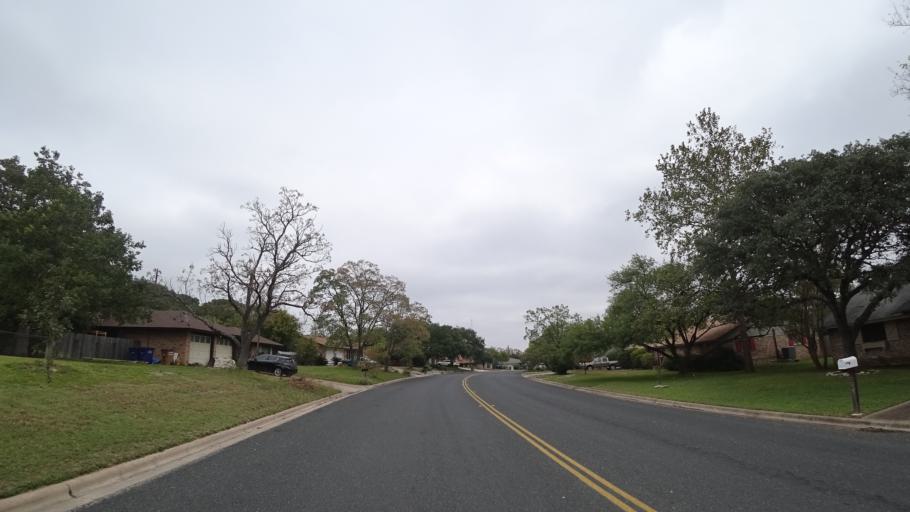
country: US
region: Texas
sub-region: Travis County
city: Barton Creek
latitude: 30.2371
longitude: -97.8825
